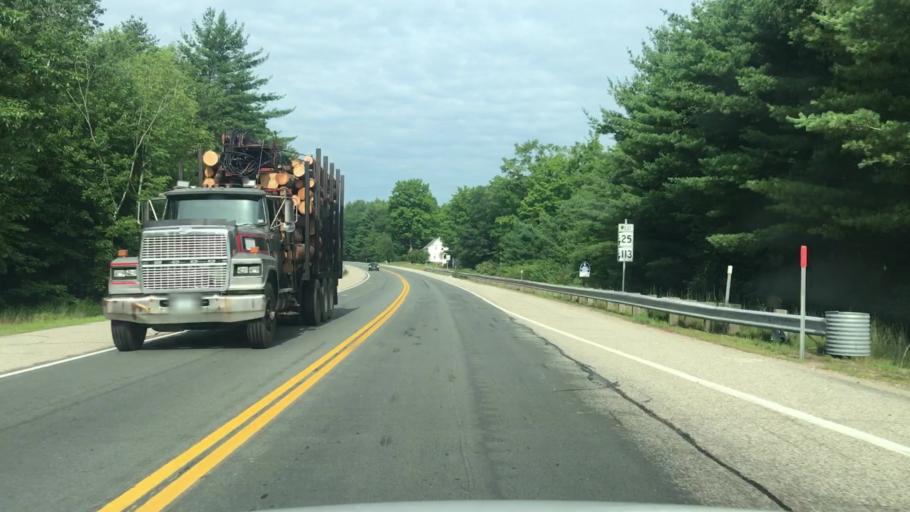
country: US
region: New Hampshire
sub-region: Carroll County
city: Tamworth
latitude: 43.8304
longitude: -71.2735
